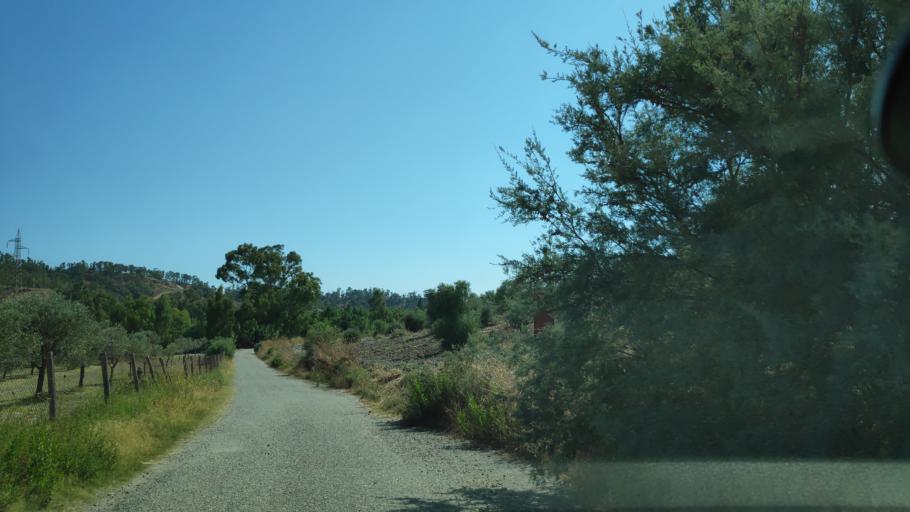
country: IT
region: Calabria
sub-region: Provincia di Reggio Calabria
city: Monasterace
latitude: 38.4297
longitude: 16.5243
